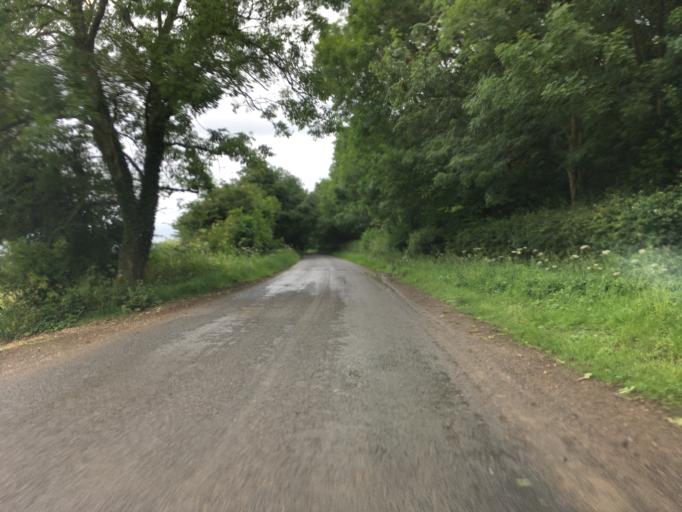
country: GB
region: England
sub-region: Gloucestershire
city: Mickleton
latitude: 52.0822
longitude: -1.7170
